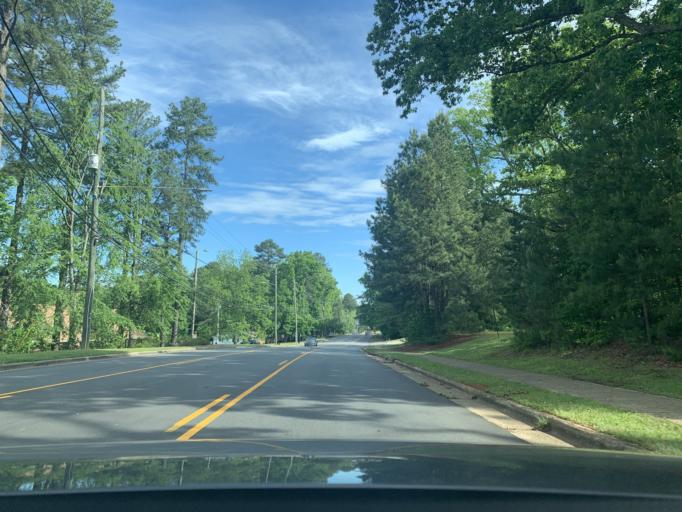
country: US
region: North Carolina
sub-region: Wake County
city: Garner
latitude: 35.7442
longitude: -78.6071
